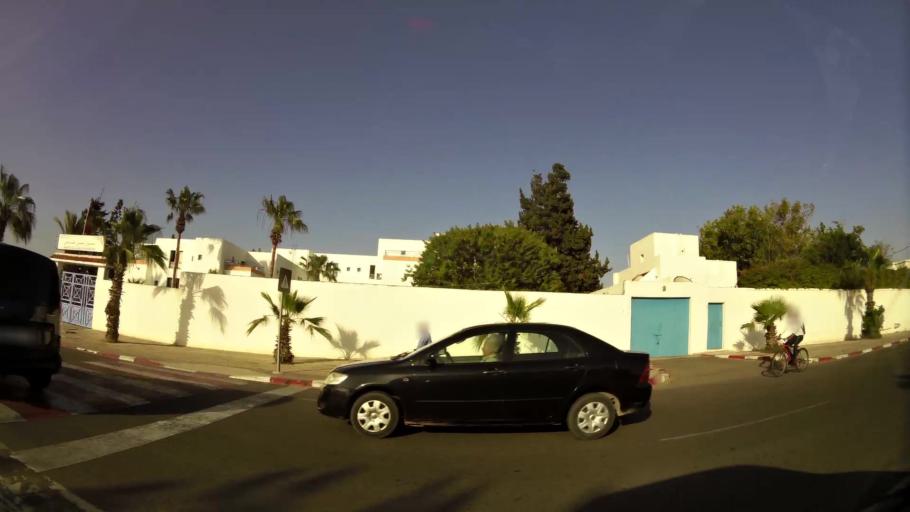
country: MA
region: Souss-Massa-Draa
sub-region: Agadir-Ida-ou-Tnan
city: Agadir
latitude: 30.4051
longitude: -9.5794
